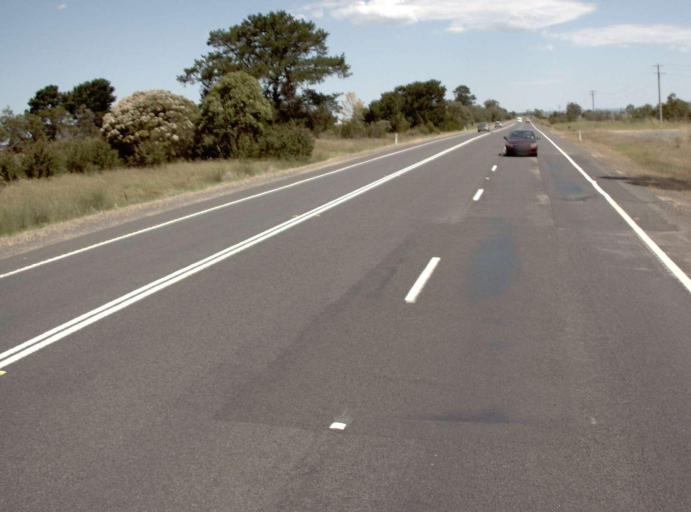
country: AU
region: Victoria
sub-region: Wellington
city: Sale
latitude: -38.0193
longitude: 147.0603
